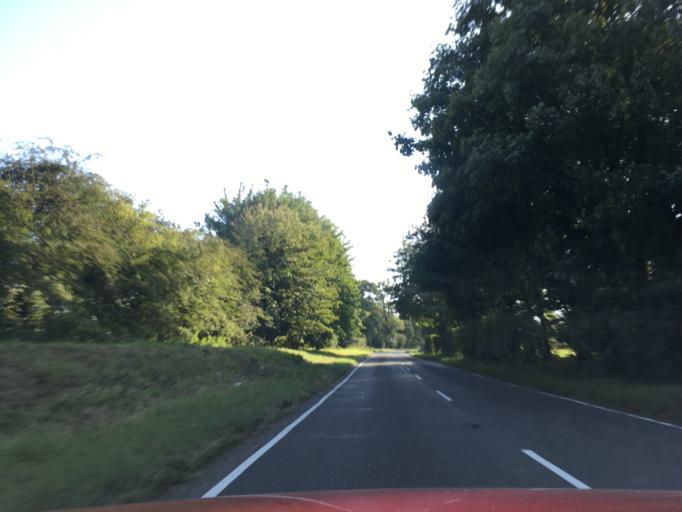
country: GB
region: England
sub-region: Hampshire
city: Four Marks
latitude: 51.0947
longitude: -0.9963
